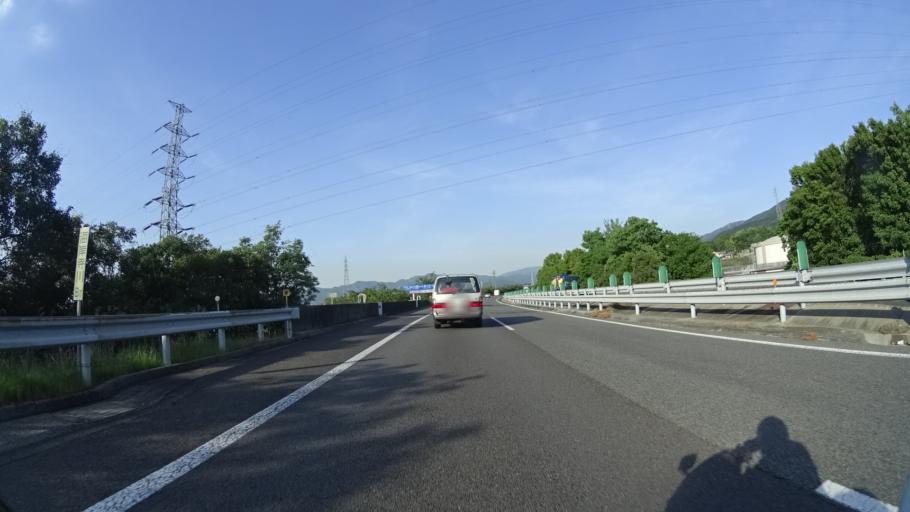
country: JP
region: Ehime
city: Kawanoecho
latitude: 33.9746
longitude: 133.5594
